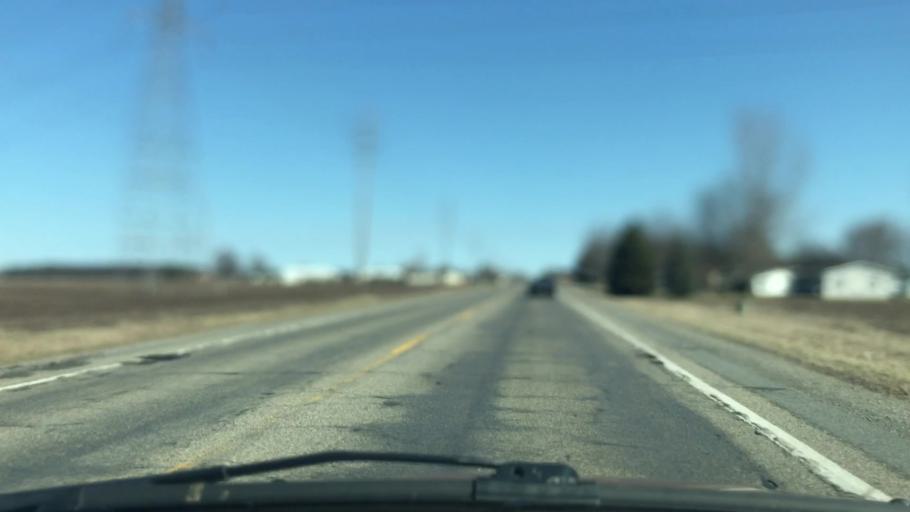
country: US
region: Indiana
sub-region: Porter County
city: Kouts
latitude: 41.3810
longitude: -87.0271
